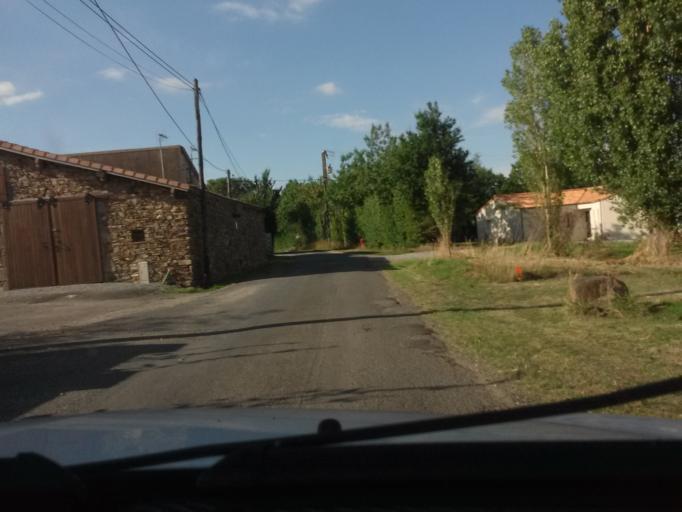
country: FR
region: Pays de la Loire
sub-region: Departement de la Loire-Atlantique
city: Vieillevigne
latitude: 46.9862
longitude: -1.4027
